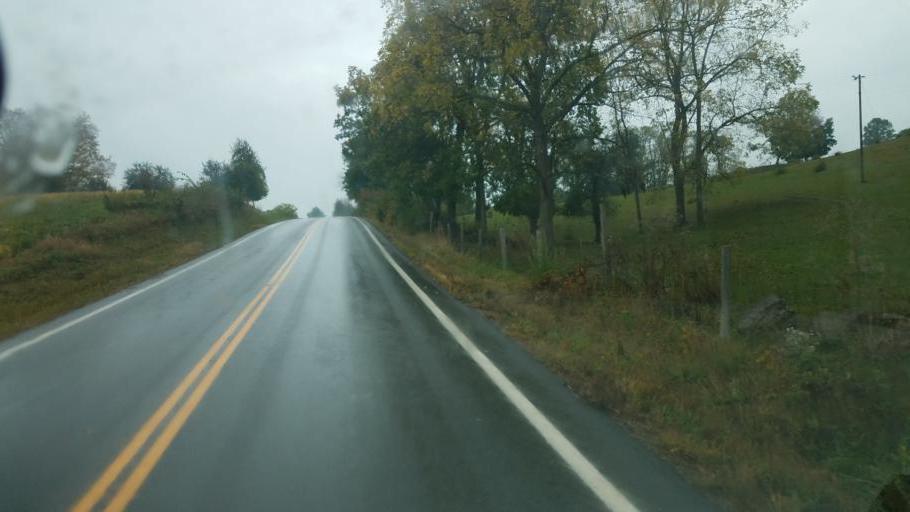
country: US
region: Ohio
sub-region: Richland County
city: Lincoln Heights
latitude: 40.6872
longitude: -82.3783
